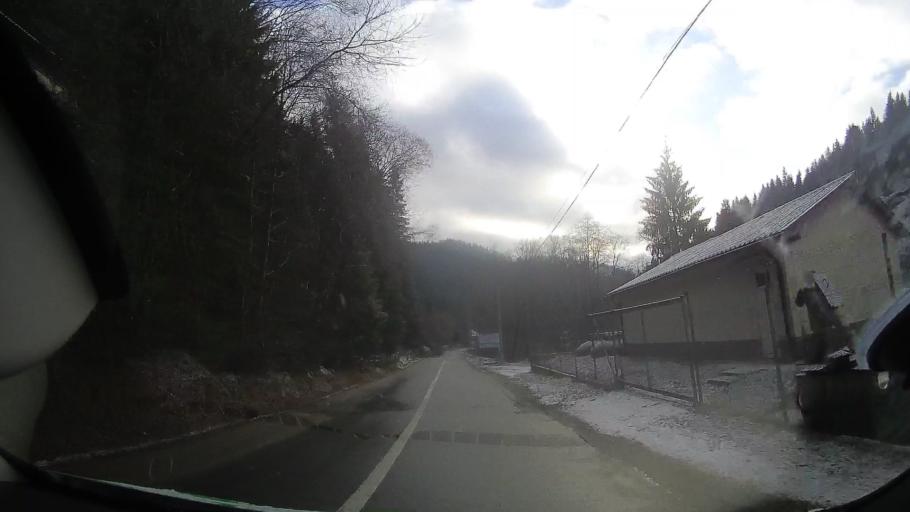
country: RO
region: Alba
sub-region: Comuna Horea
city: Horea
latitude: 46.4960
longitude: 22.9579
